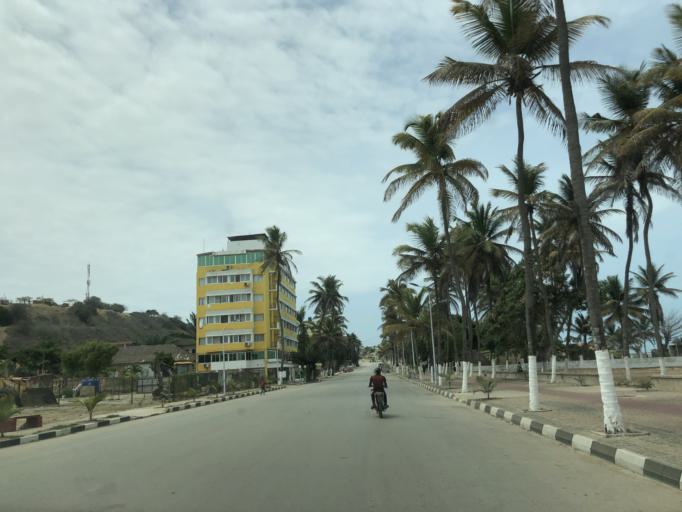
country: AO
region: Cuanza Sul
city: Sumbe
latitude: -11.1971
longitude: 13.8354
